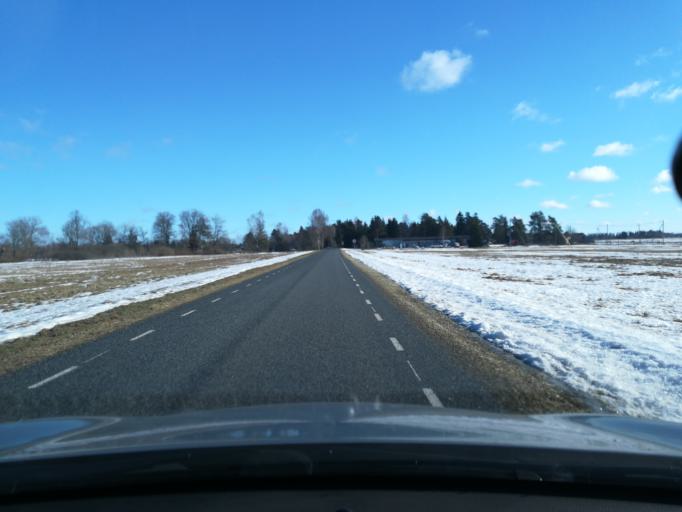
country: EE
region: Raplamaa
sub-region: Kohila vald
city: Kohila
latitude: 59.2296
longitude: 24.7417
